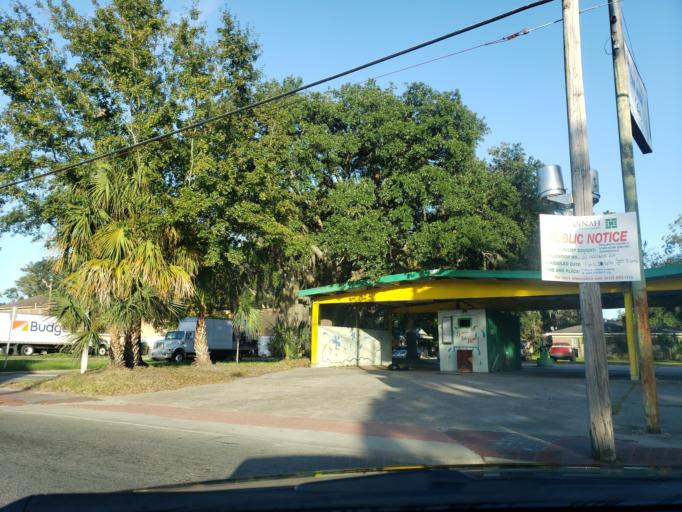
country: US
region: Georgia
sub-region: Chatham County
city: Savannah
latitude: 32.0538
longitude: -81.0833
